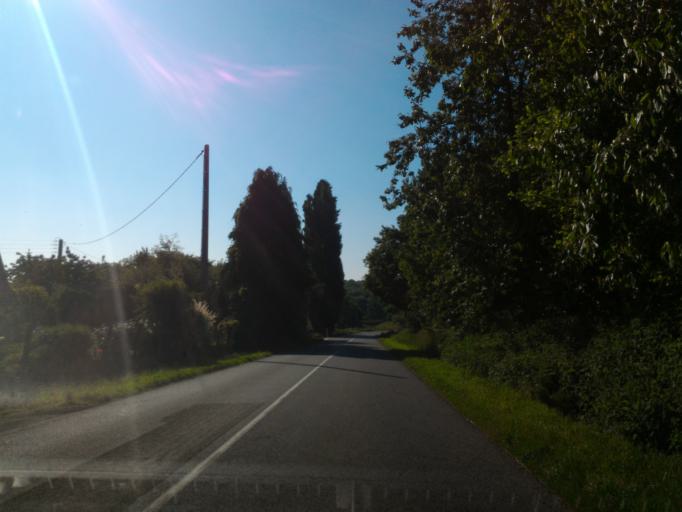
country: FR
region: Pays de la Loire
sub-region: Departement de la Mayenne
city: Juvigne
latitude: 48.1984
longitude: -1.0455
